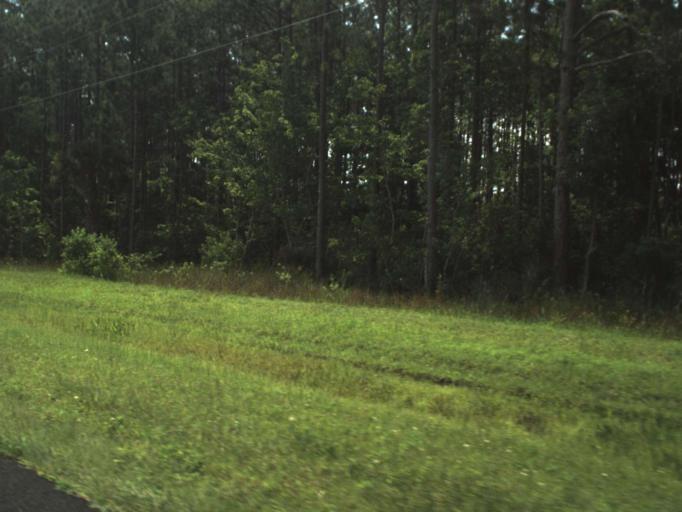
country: US
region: Florida
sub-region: Volusia County
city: Glencoe
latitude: 29.0120
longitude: -81.0209
